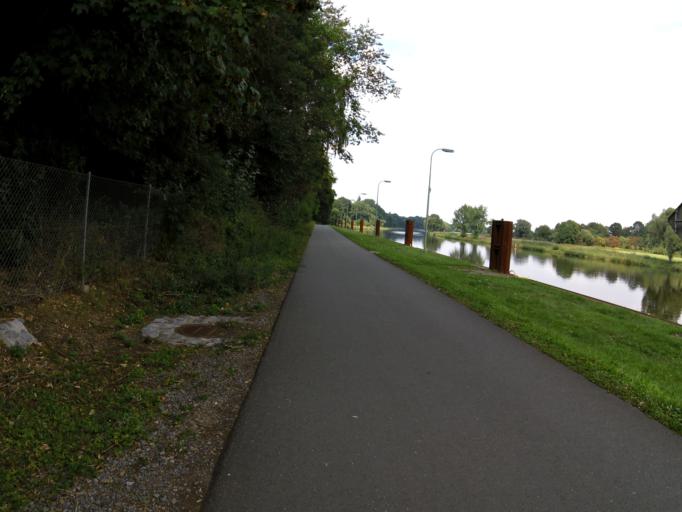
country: DE
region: North Rhine-Westphalia
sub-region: Regierungsbezirk Detmold
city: Minden
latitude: 52.3123
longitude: 8.9195
